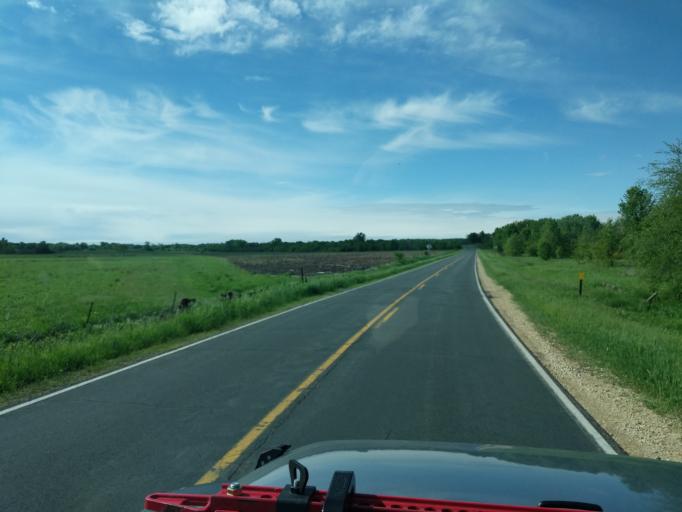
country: US
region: Wisconsin
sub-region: Saint Croix County
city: Hammond
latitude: 44.9048
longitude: -92.4860
